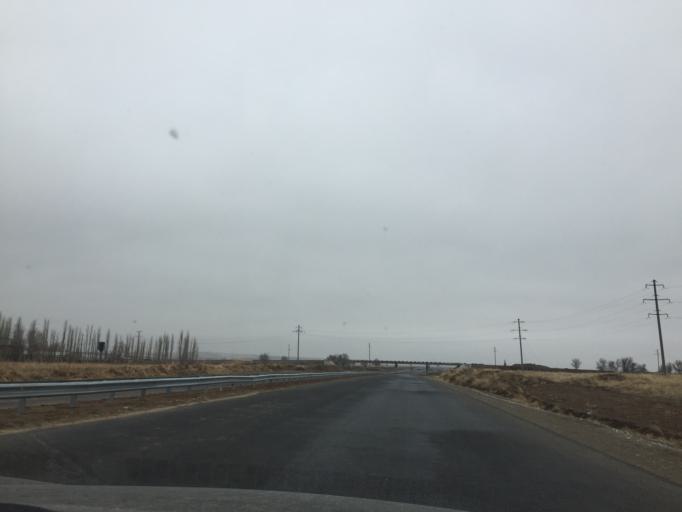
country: KZ
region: Ongtustik Qazaqstan
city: Turar Ryskulov
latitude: 42.5235
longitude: 70.3151
